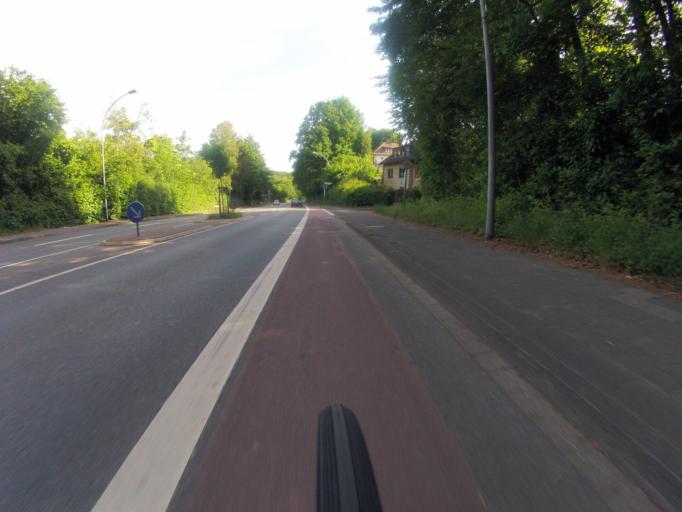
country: DE
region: North Rhine-Westphalia
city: Ibbenburen
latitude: 52.2859
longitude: 7.7232
